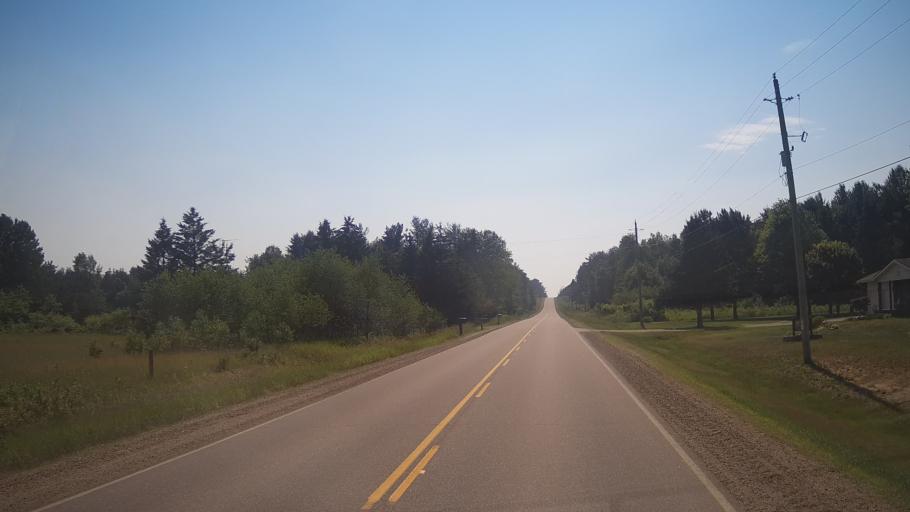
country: CA
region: Ontario
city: Pembroke
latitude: 45.6220
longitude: -77.1583
